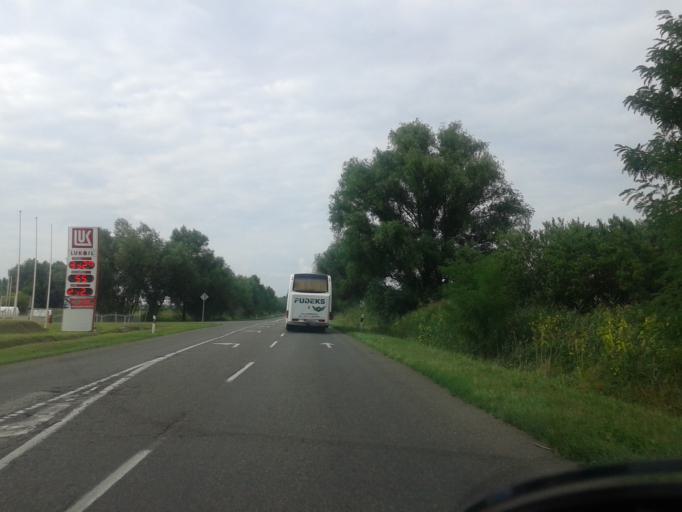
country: HU
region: Bacs-Kiskun
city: Soltvadkert
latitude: 46.5647
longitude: 19.4099
